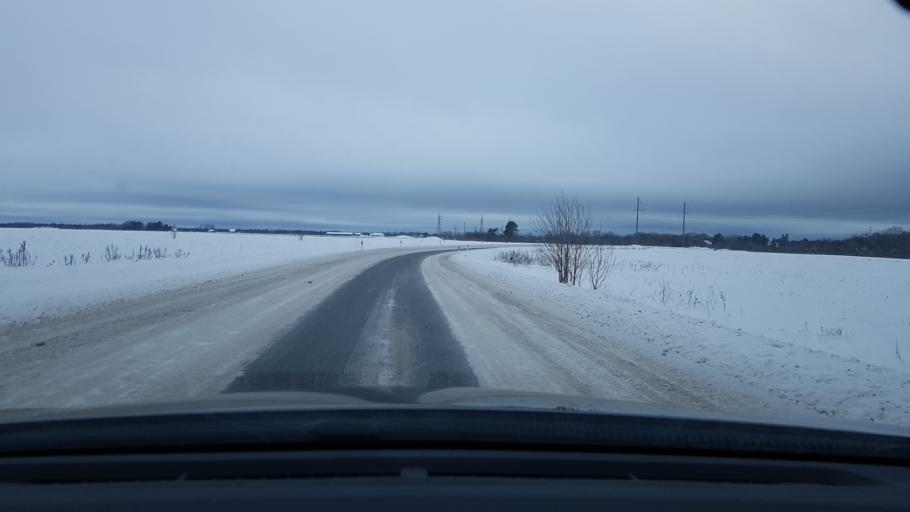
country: EE
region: Harju
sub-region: Harku vald
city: Tabasalu
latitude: 59.3917
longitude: 24.5512
